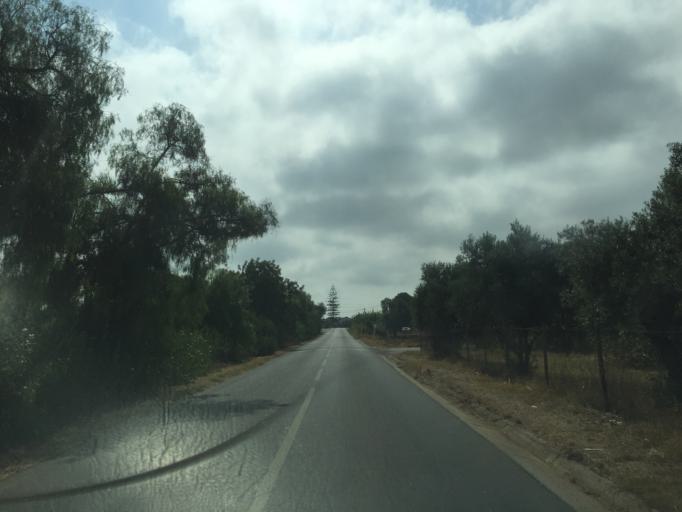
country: PT
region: Faro
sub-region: Olhao
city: Olhao
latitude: 37.0748
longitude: -7.8891
